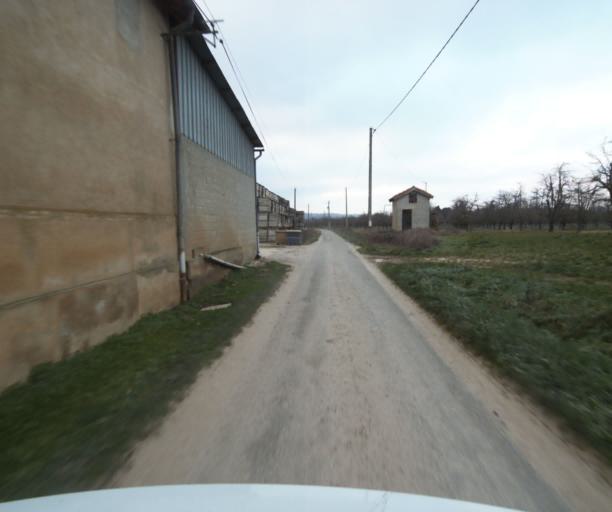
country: FR
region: Midi-Pyrenees
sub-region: Departement du Tarn-et-Garonne
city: Moissac
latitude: 44.0982
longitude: 1.1242
